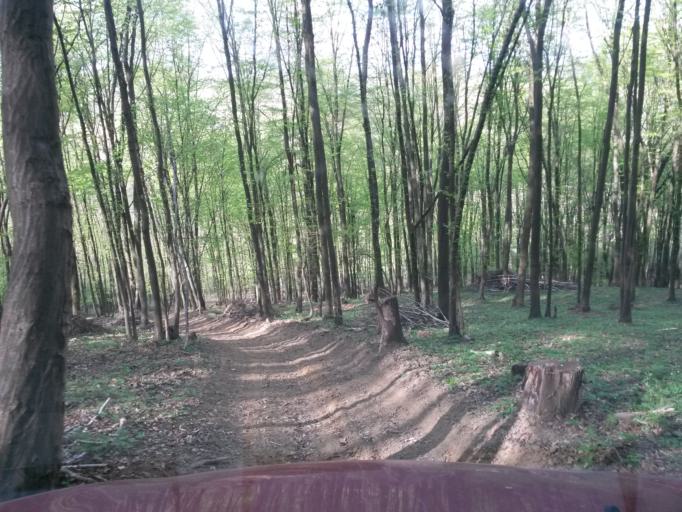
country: SK
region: Presovsky
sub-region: Okres Presov
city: Presov
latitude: 48.9527
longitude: 21.1502
